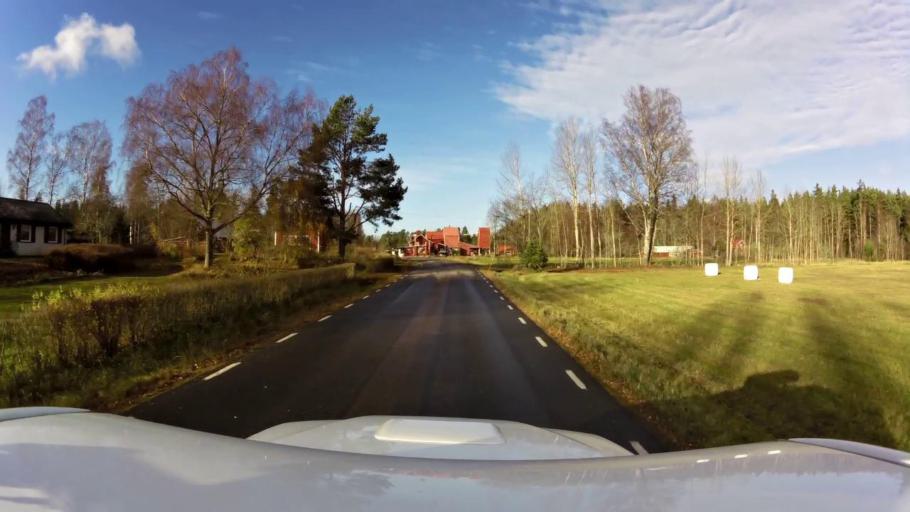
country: SE
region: OEstergoetland
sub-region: Linkopings Kommun
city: Linkoping
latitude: 58.3253
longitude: 15.6438
